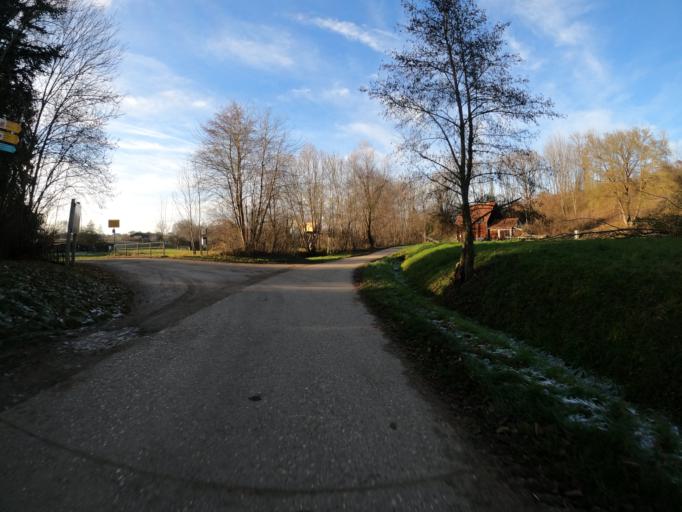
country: DE
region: Baden-Wuerttemberg
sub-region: Regierungsbezirk Stuttgart
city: Zell unter Aichelberg
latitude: 48.6540
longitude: 9.5866
